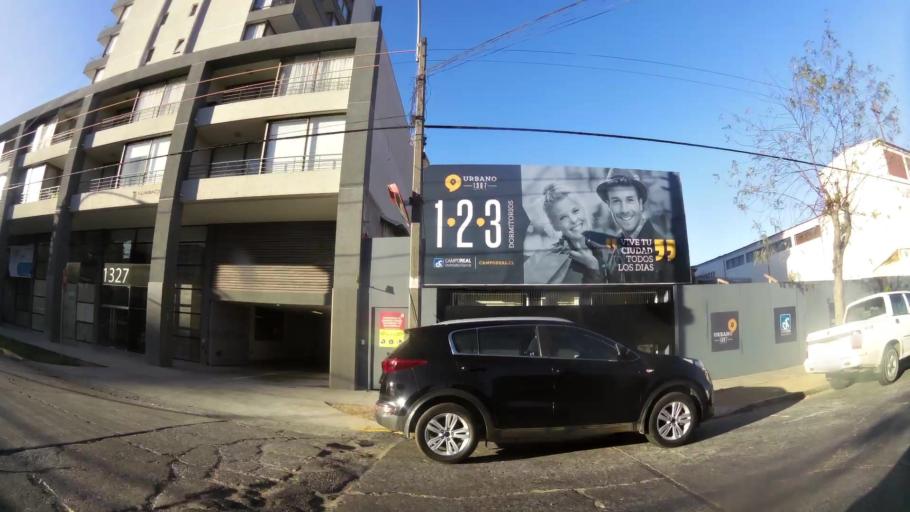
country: CL
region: Valparaiso
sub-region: Provincia de Valparaiso
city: Vina del Mar
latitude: -33.0264
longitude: -71.5431
